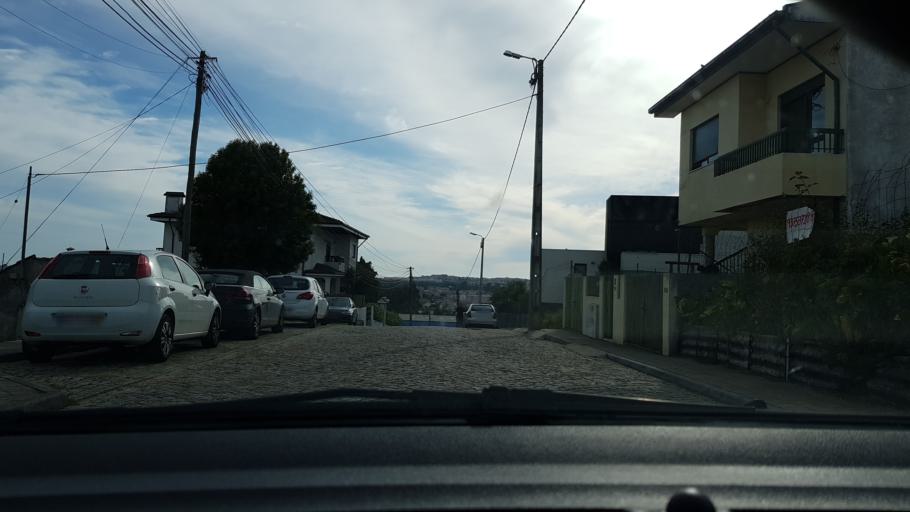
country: PT
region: Porto
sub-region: Gondomar
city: Baguim do Monte
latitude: 41.1929
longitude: -8.5434
